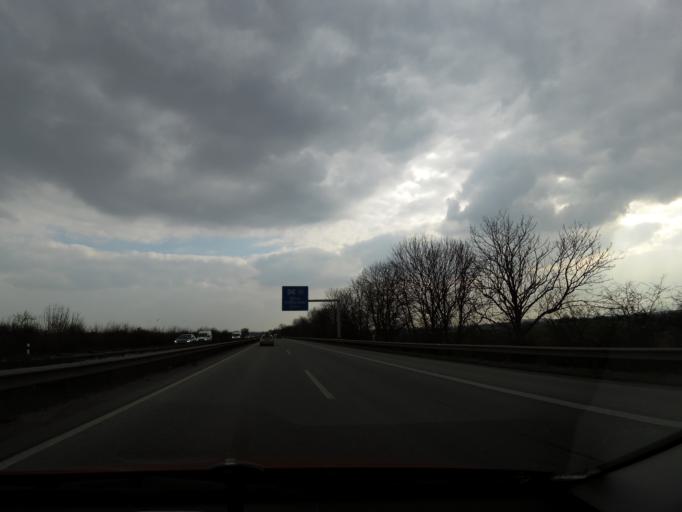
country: DE
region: Rheinland-Pfalz
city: Heuchelheim bei Frankenthal
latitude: 49.5763
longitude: 8.2970
